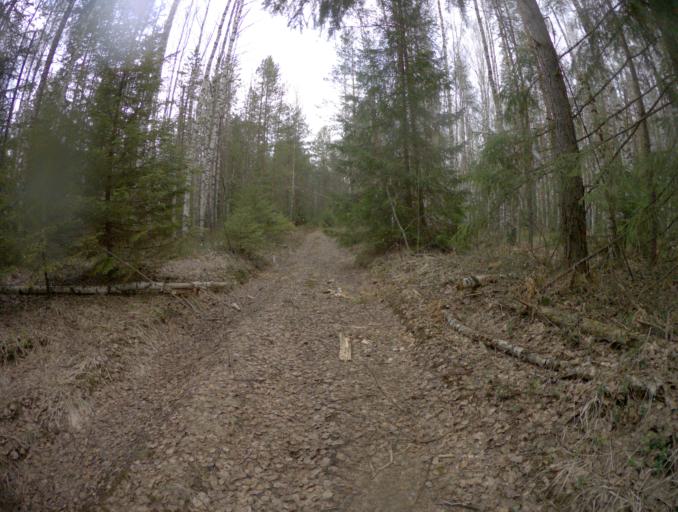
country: RU
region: Vladimir
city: Raduzhnyy
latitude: 55.9540
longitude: 40.2707
